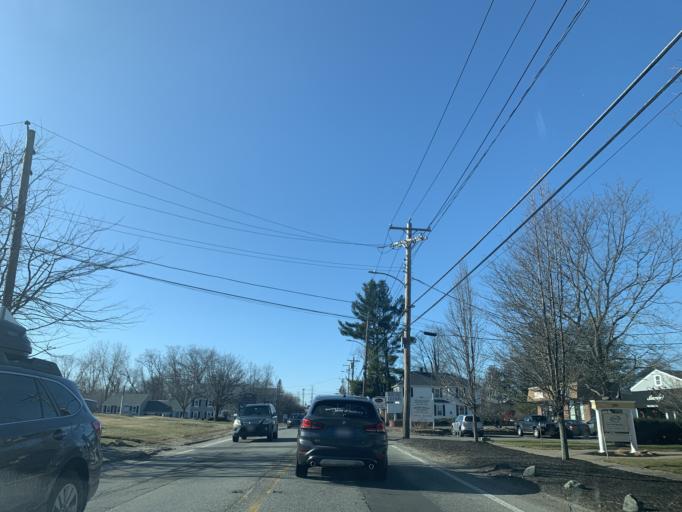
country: US
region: Massachusetts
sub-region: Middlesex County
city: Wayland
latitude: 42.3632
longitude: -71.3640
